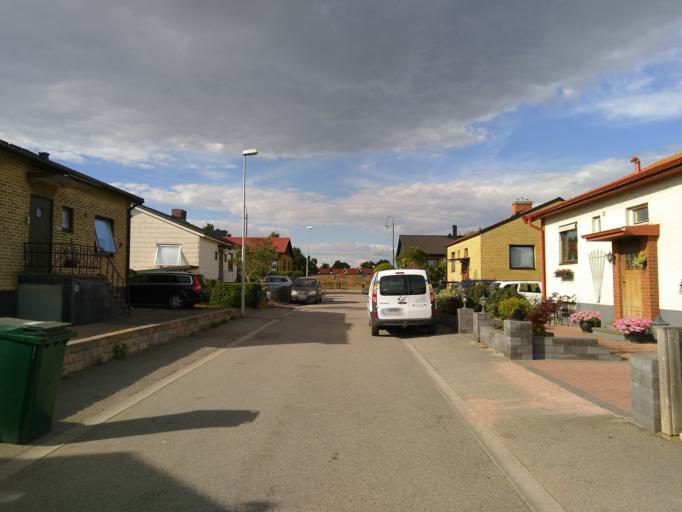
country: SE
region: Skane
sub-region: Landskrona
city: Landskrona
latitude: 55.8780
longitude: 12.8523
